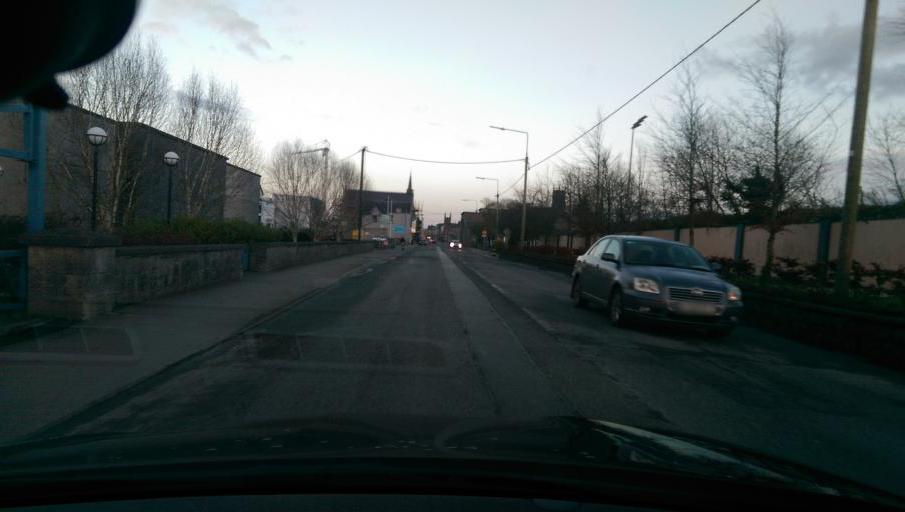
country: IE
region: Connaught
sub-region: County Galway
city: Ballinasloe
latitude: 53.3318
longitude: -8.2297
